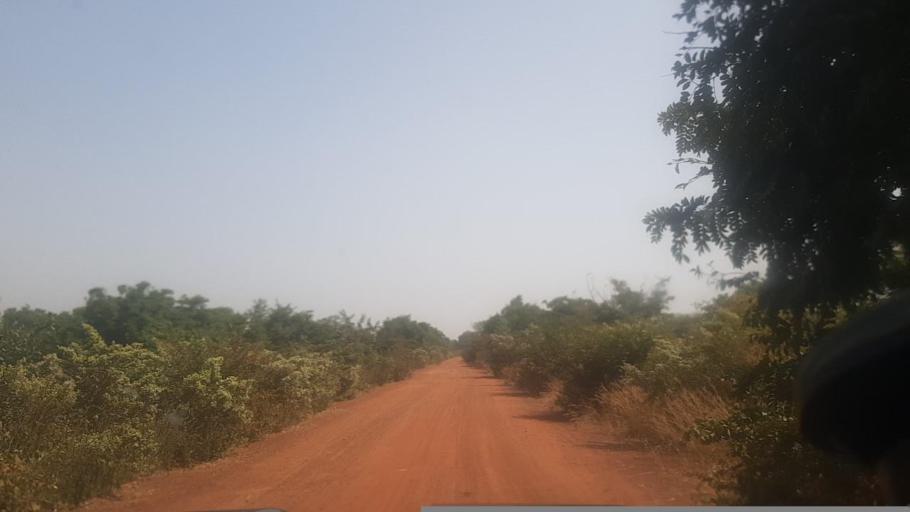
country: ML
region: Segou
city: Bla
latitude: 12.9220
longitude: -6.2619
